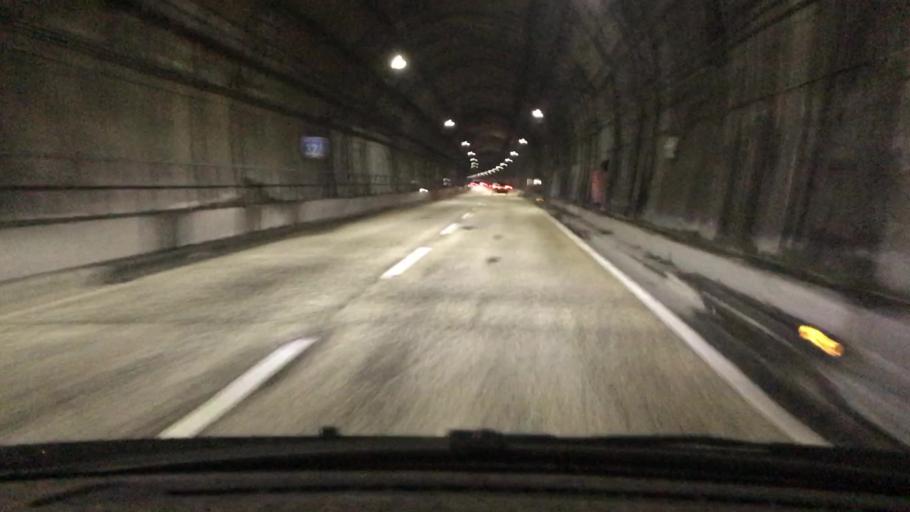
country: JP
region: Hyogo
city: Kobe
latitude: 34.7239
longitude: 135.1839
